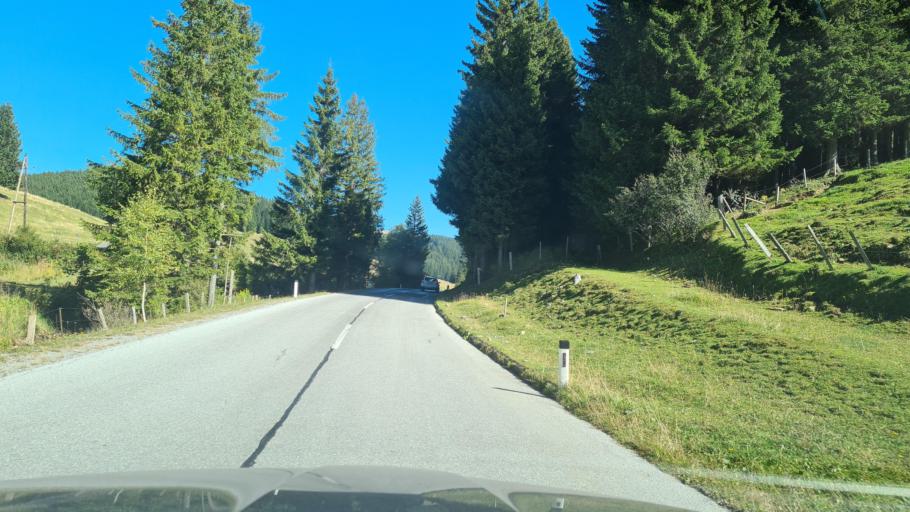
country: AT
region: Styria
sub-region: Politischer Bezirk Weiz
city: Gasen
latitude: 47.3512
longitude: 15.5186
